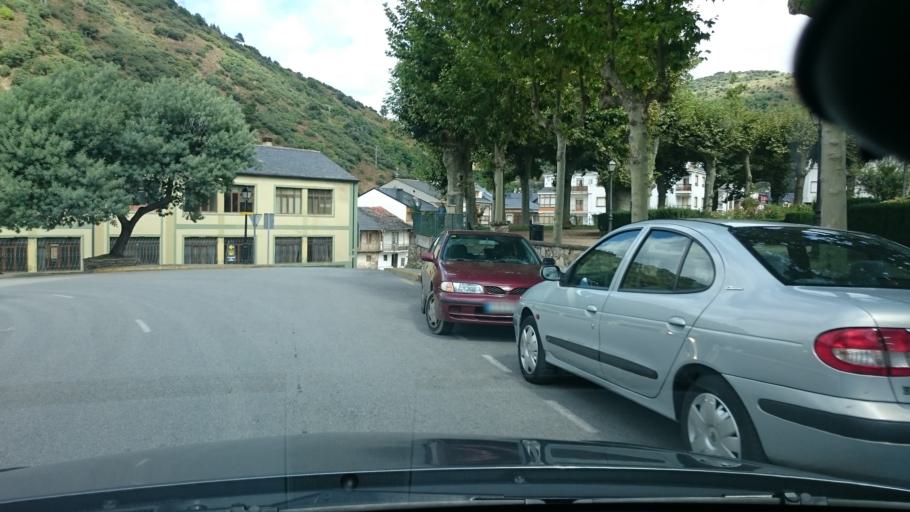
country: ES
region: Castille and Leon
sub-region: Provincia de Leon
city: Villafranca del Bierzo
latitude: 42.6095
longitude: -6.8085
